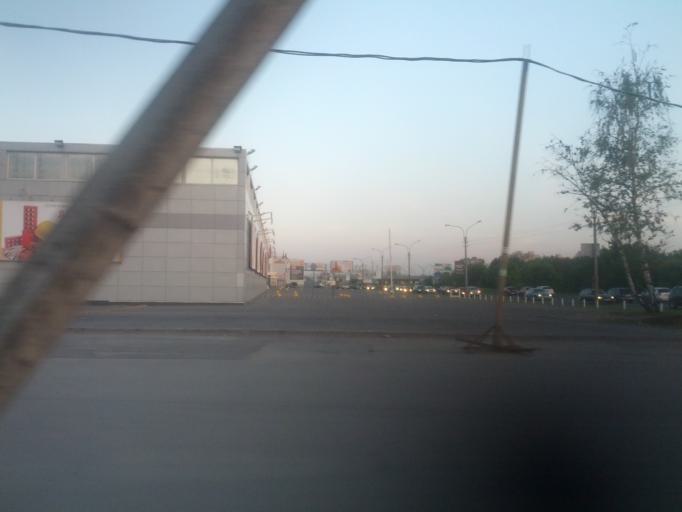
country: RU
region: St.-Petersburg
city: Staraya Derevnya
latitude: 59.9977
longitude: 30.2345
